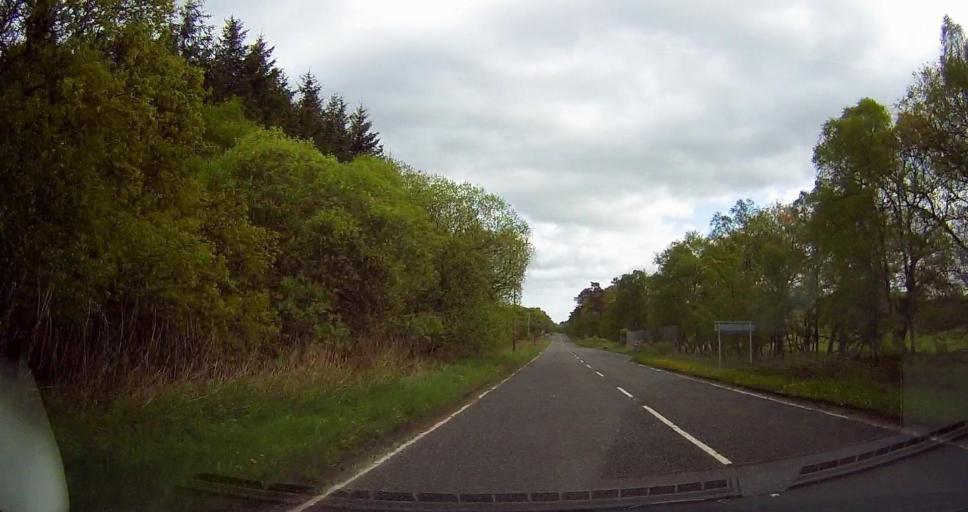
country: GB
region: Scotland
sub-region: Clackmannanshire
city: Dollar
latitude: 56.1579
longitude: -3.6159
